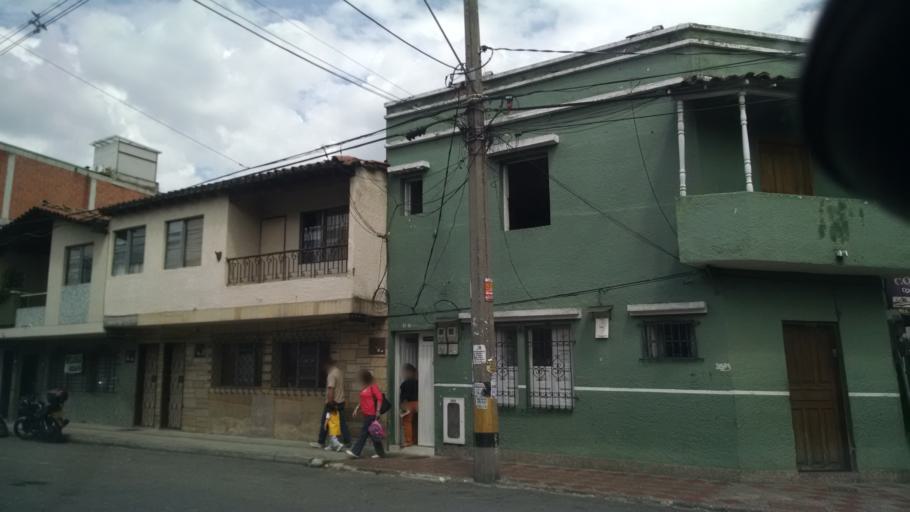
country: CO
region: Antioquia
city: Medellin
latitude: 6.2478
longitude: -75.5844
